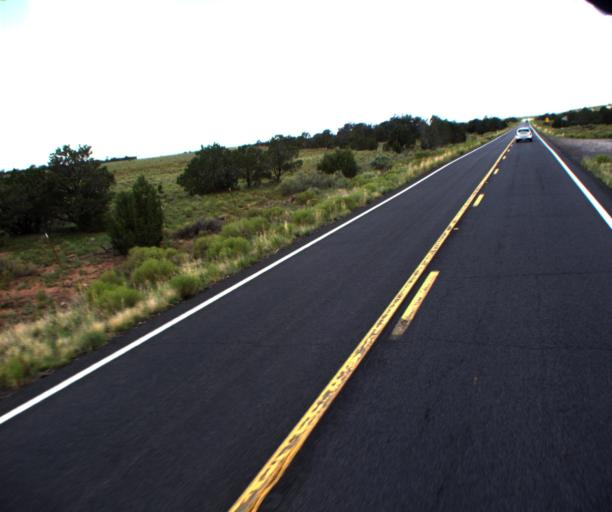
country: US
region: Arizona
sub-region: Coconino County
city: Parks
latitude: 35.5841
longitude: -111.9755
